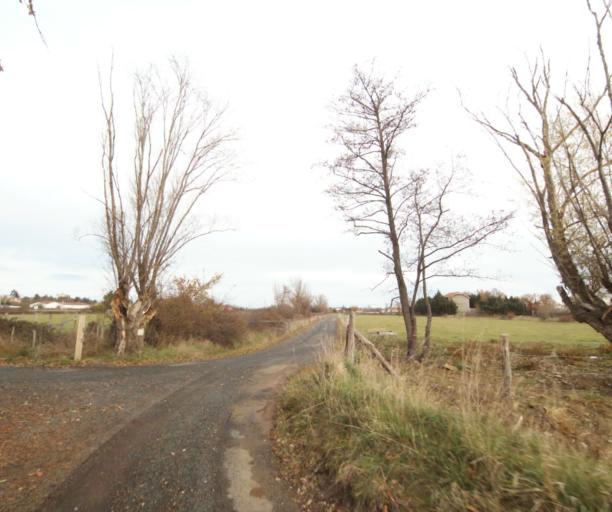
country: FR
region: Rhone-Alpes
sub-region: Departement de la Loire
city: Sury-le-Comtal
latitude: 45.5285
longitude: 4.1997
